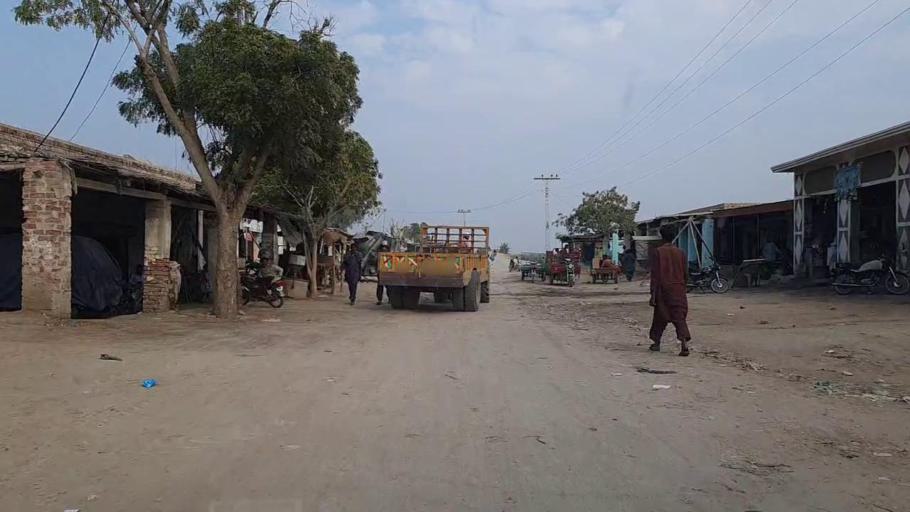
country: PK
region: Sindh
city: Mirwah Gorchani
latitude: 25.4260
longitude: 69.1550
